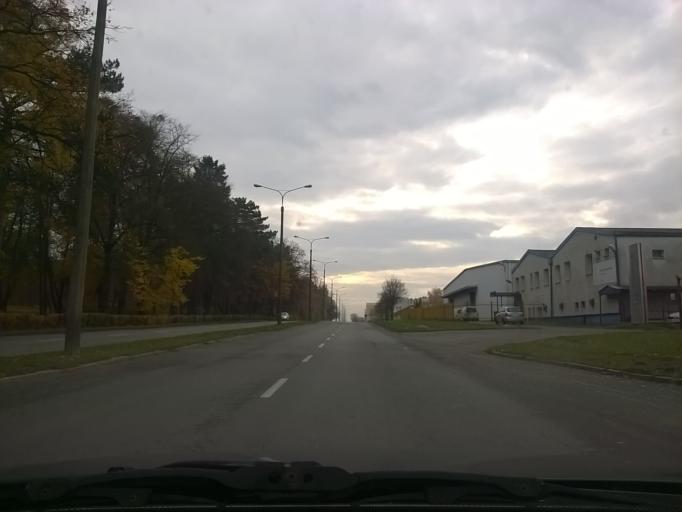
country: PL
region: Warmian-Masurian Voivodeship
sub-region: Powiat elblaski
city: Elblag
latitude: 54.1854
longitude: 19.3887
